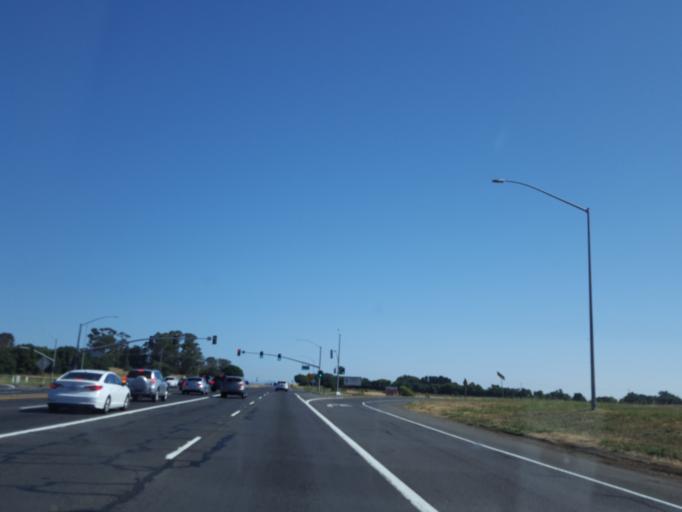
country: US
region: California
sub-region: Napa County
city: American Canyon
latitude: 38.2250
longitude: -122.2582
